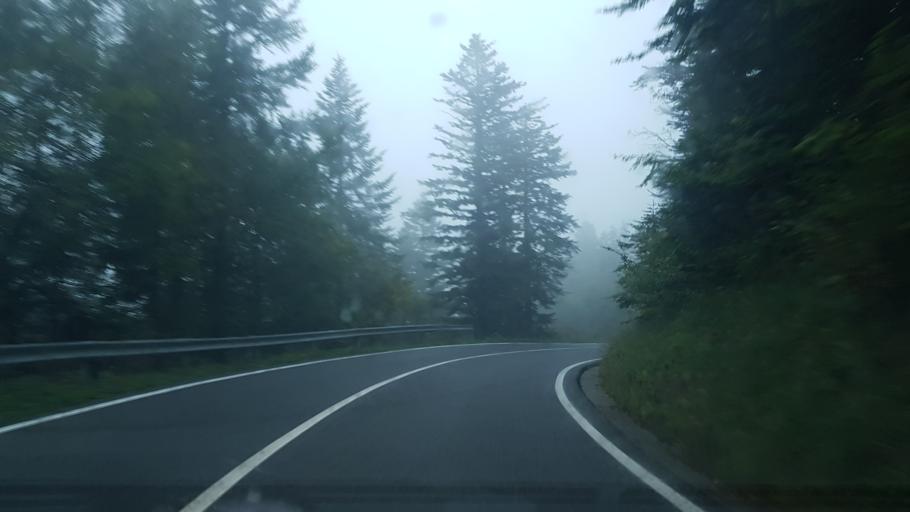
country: IT
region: Piedmont
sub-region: Provincia di Cuneo
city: Frabosa Soprana
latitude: 44.2579
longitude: 7.7745
